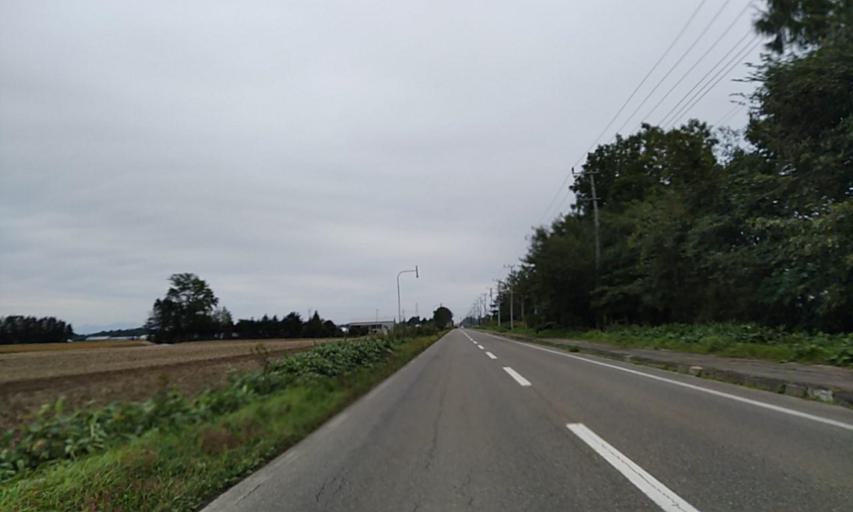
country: JP
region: Hokkaido
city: Obihiro
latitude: 42.6767
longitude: 143.1180
